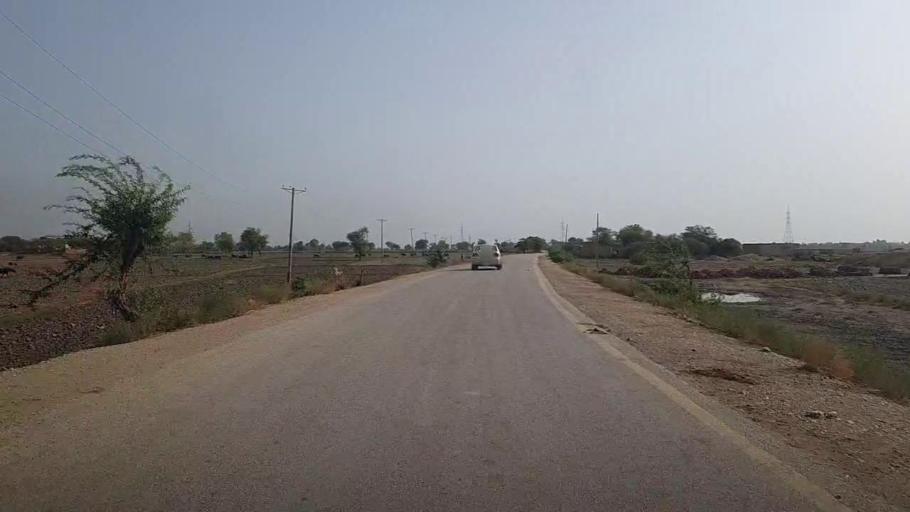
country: PK
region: Sindh
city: Khairpur Nathan Shah
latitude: 27.1004
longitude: 67.7555
